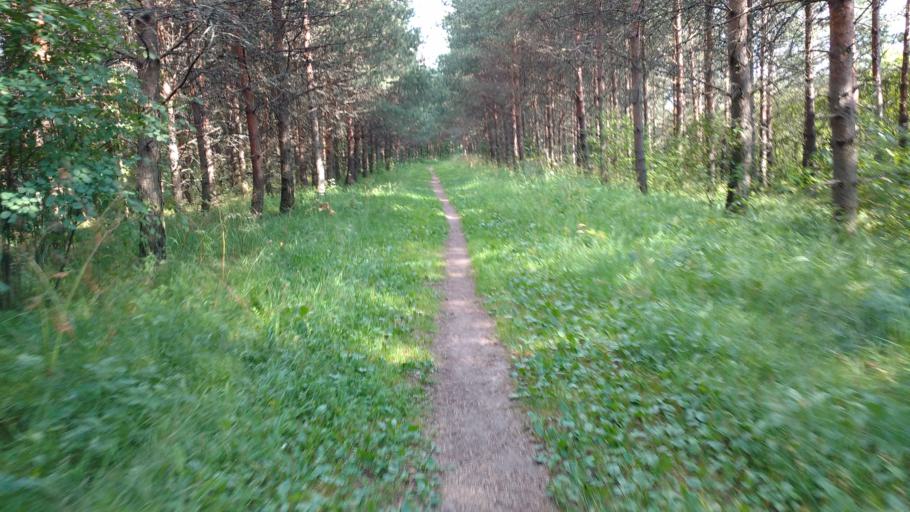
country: FI
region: Varsinais-Suomi
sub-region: Salo
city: Salo
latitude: 60.3890
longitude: 23.1603
